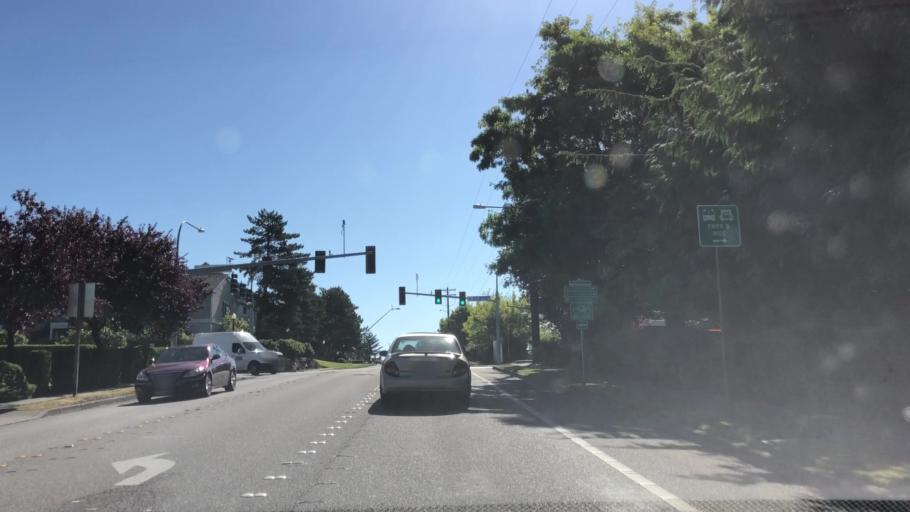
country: US
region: Washington
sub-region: Snohomish County
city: Lynnwood
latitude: 47.8174
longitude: -122.2986
